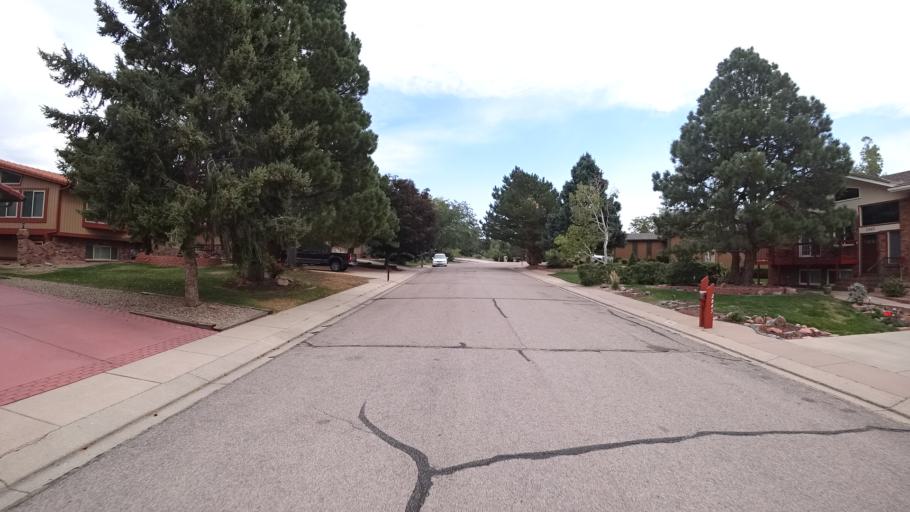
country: US
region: Colorado
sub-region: El Paso County
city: Colorado Springs
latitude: 38.8720
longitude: -104.7870
